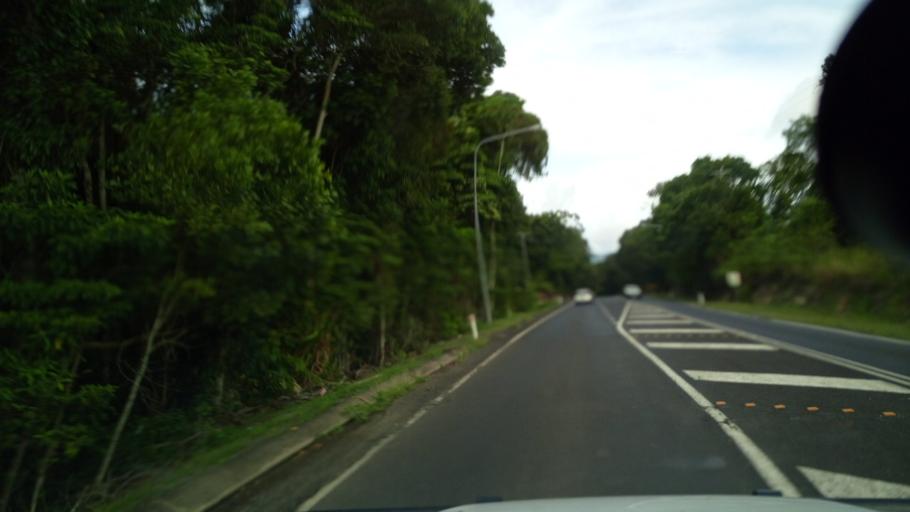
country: AU
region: Queensland
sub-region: Tablelands
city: Kuranda
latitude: -16.8160
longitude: 145.6421
